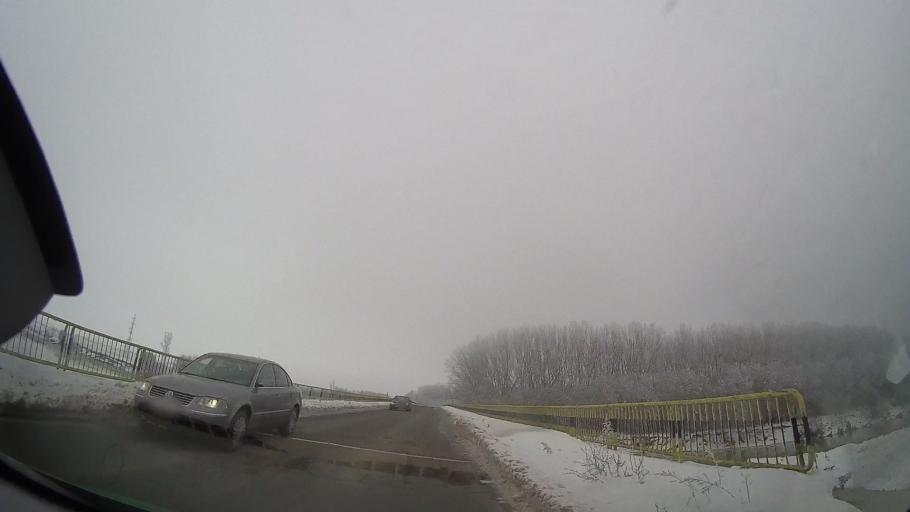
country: RO
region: Neamt
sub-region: Comuna Horia
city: Cotu Vames
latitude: 46.8819
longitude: 26.9713
